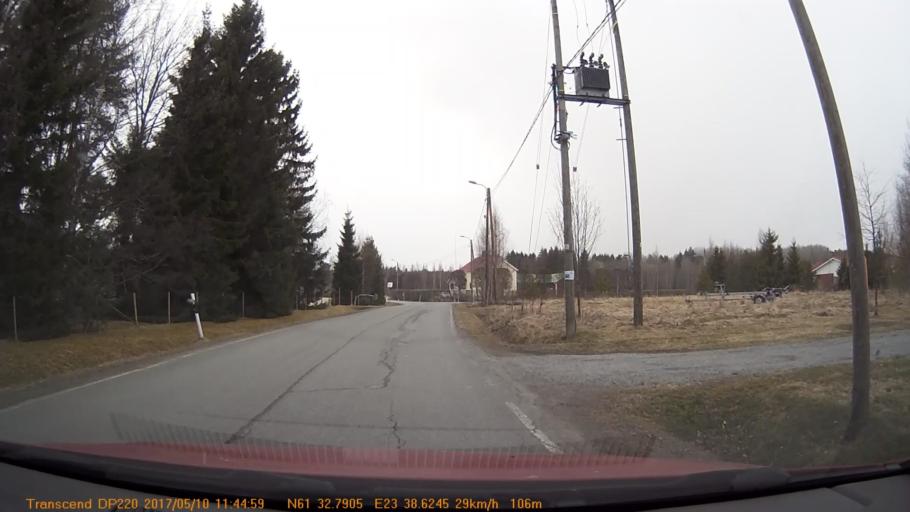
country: FI
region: Pirkanmaa
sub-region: Tampere
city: Yloejaervi
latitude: 61.5465
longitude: 23.6437
